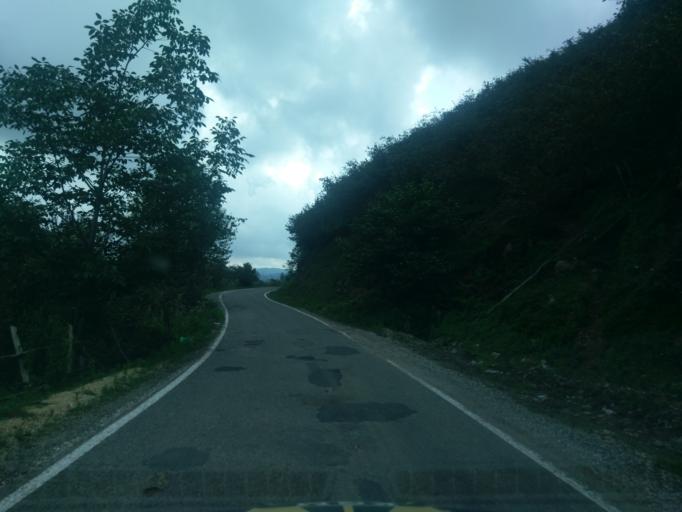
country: TR
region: Ordu
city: Camas
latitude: 40.8889
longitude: 37.6283
